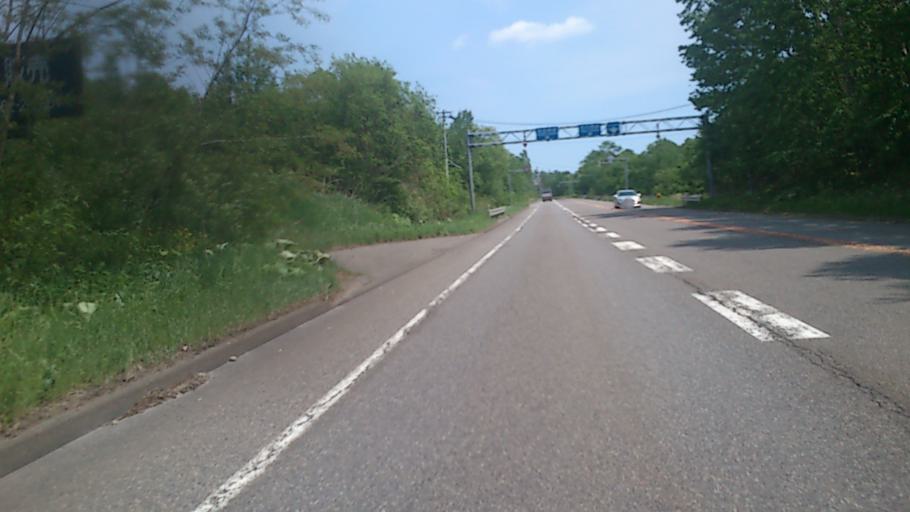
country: JP
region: Hokkaido
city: Otofuke
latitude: 43.2343
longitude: 143.4932
